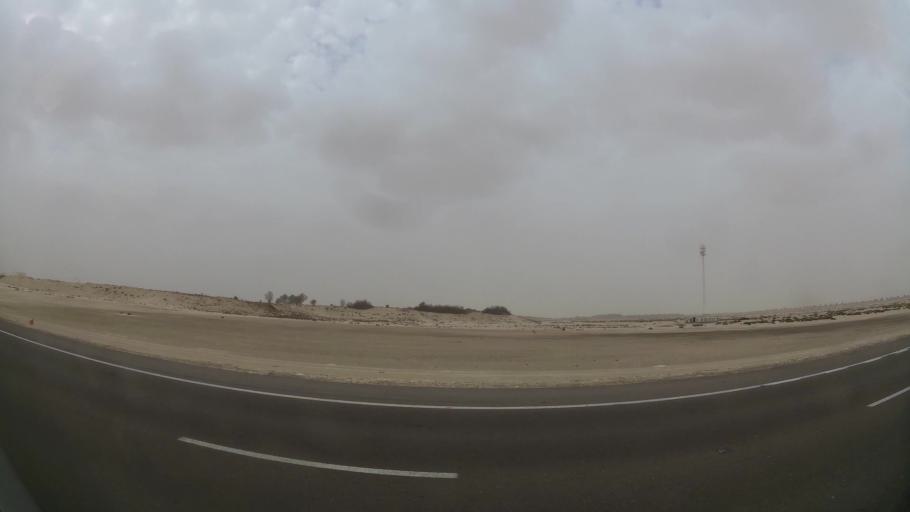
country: AE
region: Abu Dhabi
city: Abu Dhabi
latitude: 24.4045
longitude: 54.7165
